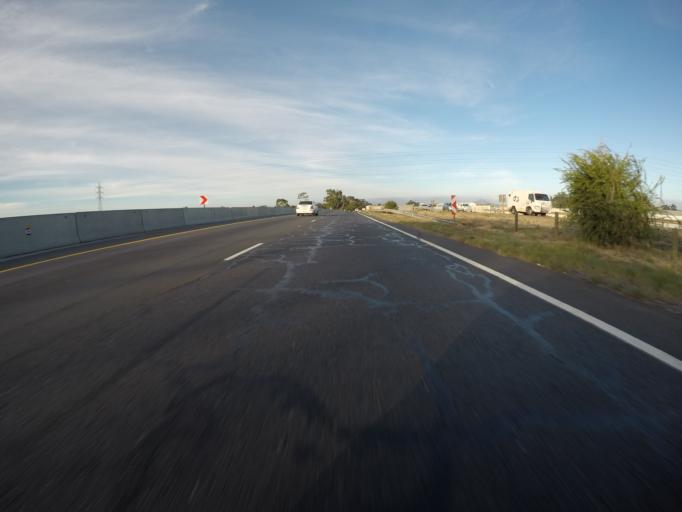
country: ZA
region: Western Cape
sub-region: City of Cape Town
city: Kraaifontein
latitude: -33.8386
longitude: 18.7253
